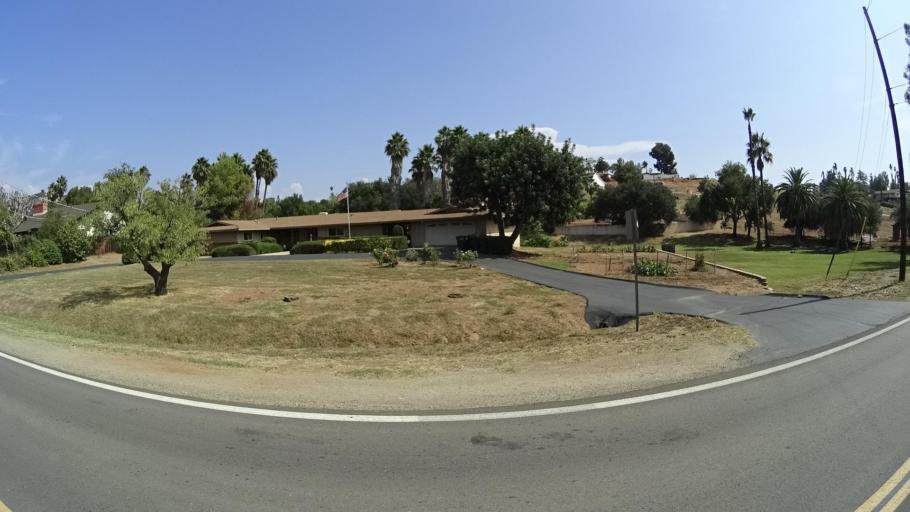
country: US
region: California
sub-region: San Diego County
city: Escondido
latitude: 33.1138
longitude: -117.0452
